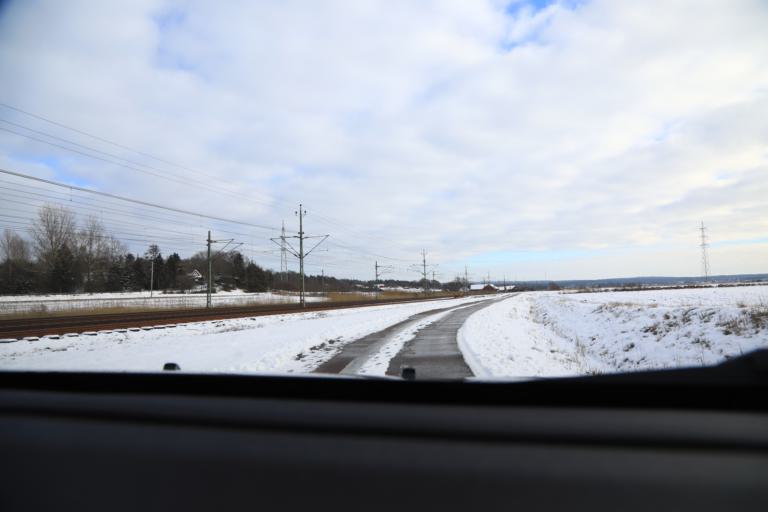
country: SE
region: Halland
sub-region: Kungsbacka Kommun
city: Frillesas
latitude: 57.2381
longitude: 12.1965
